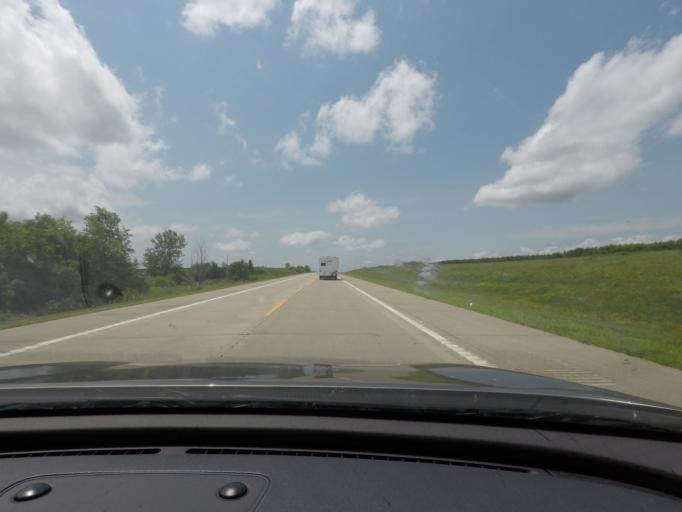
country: US
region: Missouri
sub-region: Carroll County
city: Carrollton
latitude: 39.2022
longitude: -93.4854
